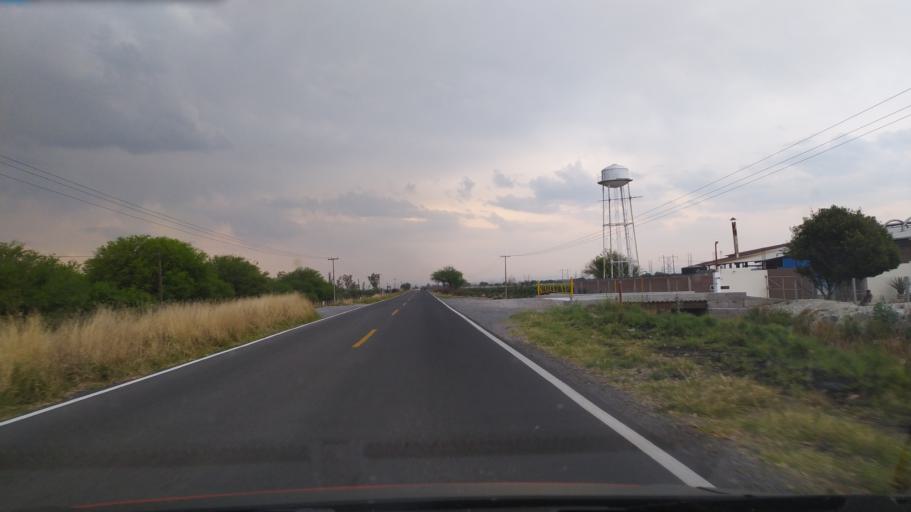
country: MX
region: Guanajuato
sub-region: San Francisco del Rincon
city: San Ignacio de Hidalgo
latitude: 20.8437
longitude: -101.8968
